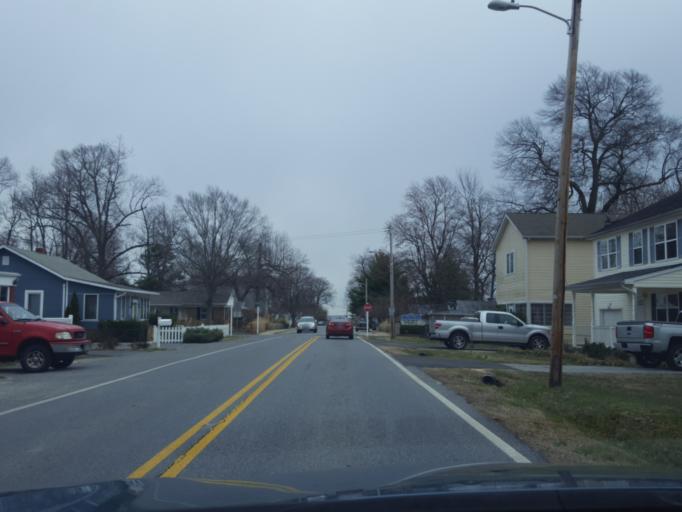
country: US
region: Maryland
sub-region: Calvert County
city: North Beach
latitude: 38.7078
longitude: -76.5383
